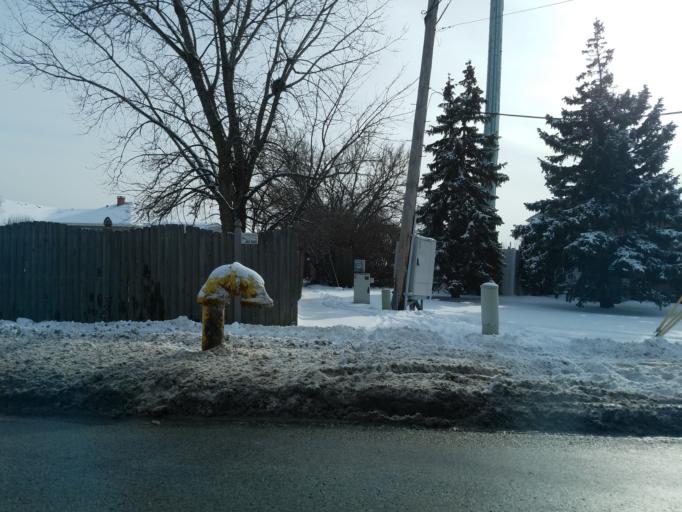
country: US
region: Illinois
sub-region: Cook County
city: Orland Park
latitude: 41.6163
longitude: -87.8330
